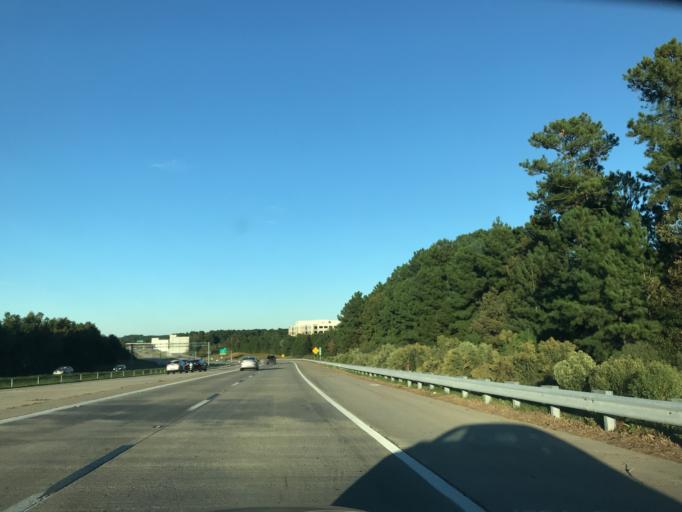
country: US
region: North Carolina
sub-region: Wake County
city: Morrisville
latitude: 35.8622
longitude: -78.8412
